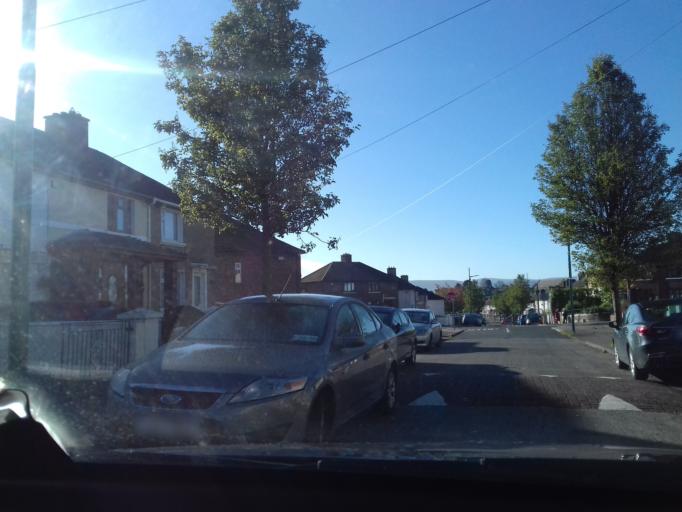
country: IE
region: Leinster
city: Cabra
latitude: 53.3696
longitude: -6.2996
